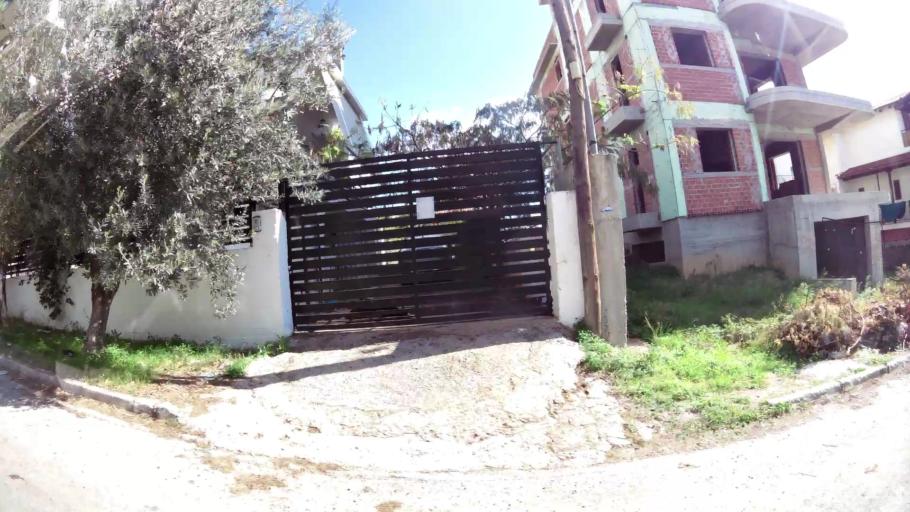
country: GR
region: Attica
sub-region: Nomarchia Anatolikis Attikis
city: Voula
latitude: 37.8444
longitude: 23.7742
